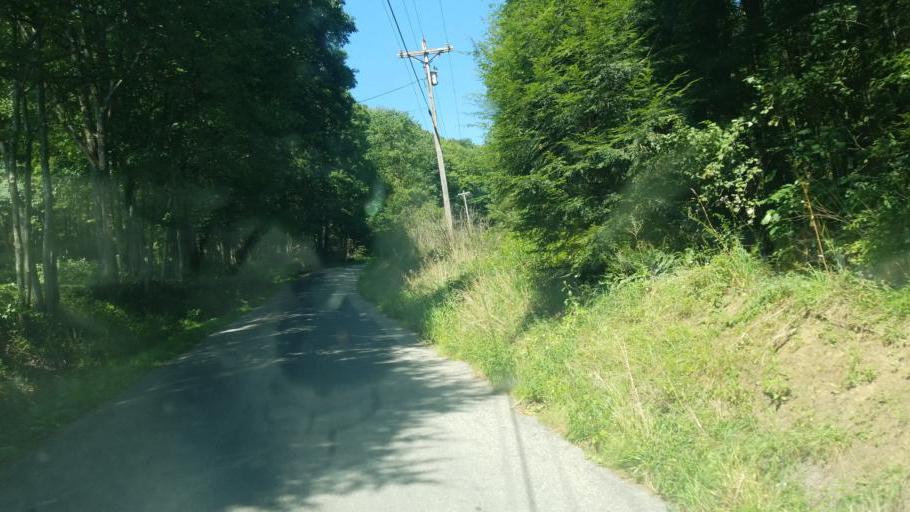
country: US
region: Pennsylvania
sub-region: Clarion County
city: Knox
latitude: 41.1911
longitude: -79.5166
